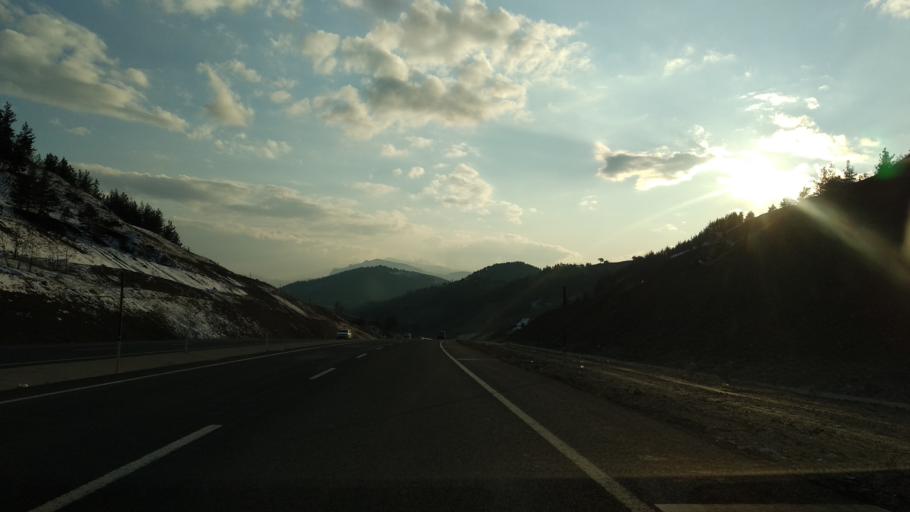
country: TR
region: Kahramanmaras
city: Yenicekale
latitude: 37.7135
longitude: 36.6940
